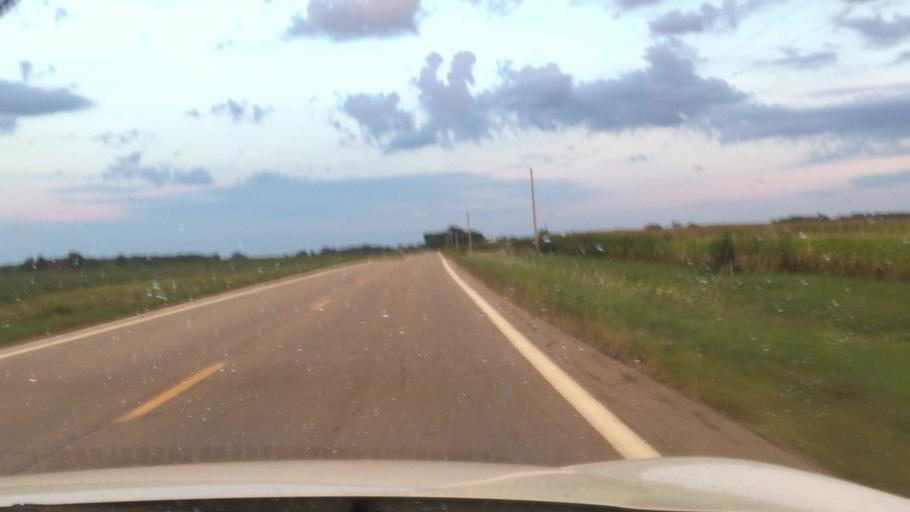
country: US
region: Ohio
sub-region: Champaign County
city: Mechanicsburg
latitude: 40.0375
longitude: -83.5026
